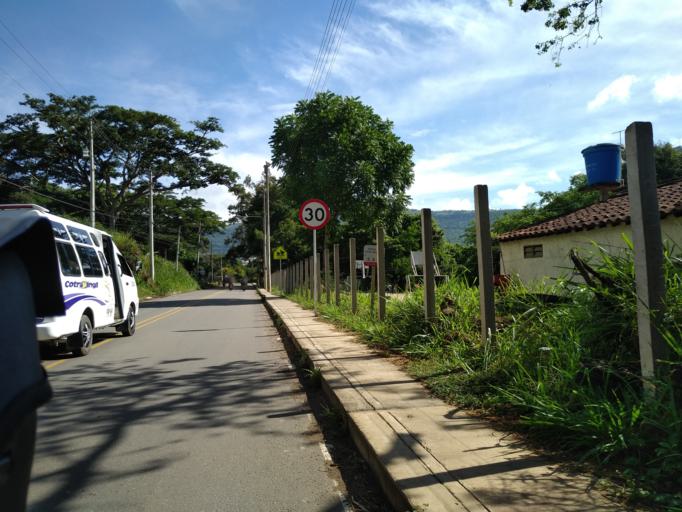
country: CO
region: Santander
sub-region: San Gil
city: San Gil
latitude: 6.5365
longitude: -73.1262
